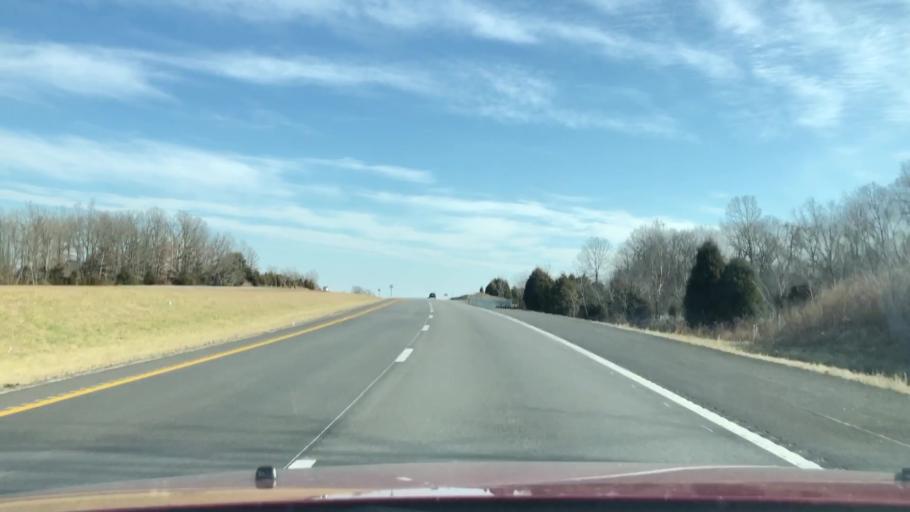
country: US
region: Missouri
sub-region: Wright County
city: Mansfield
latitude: 37.1105
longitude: -92.6414
